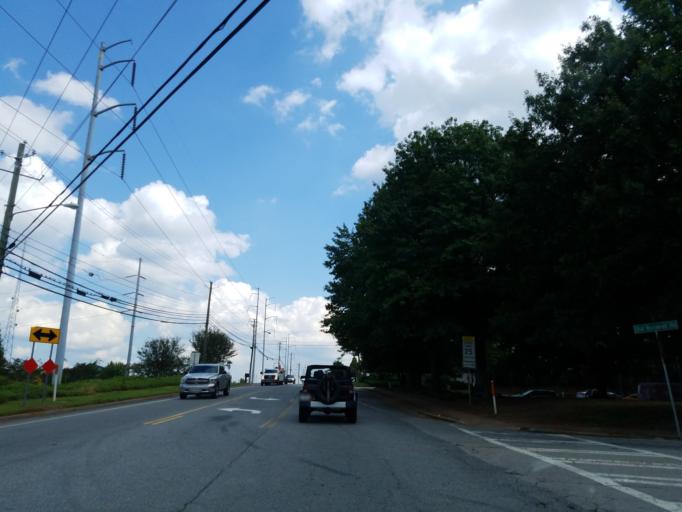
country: US
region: Georgia
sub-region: Fulton County
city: Alpharetta
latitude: 34.0608
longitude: -84.3089
